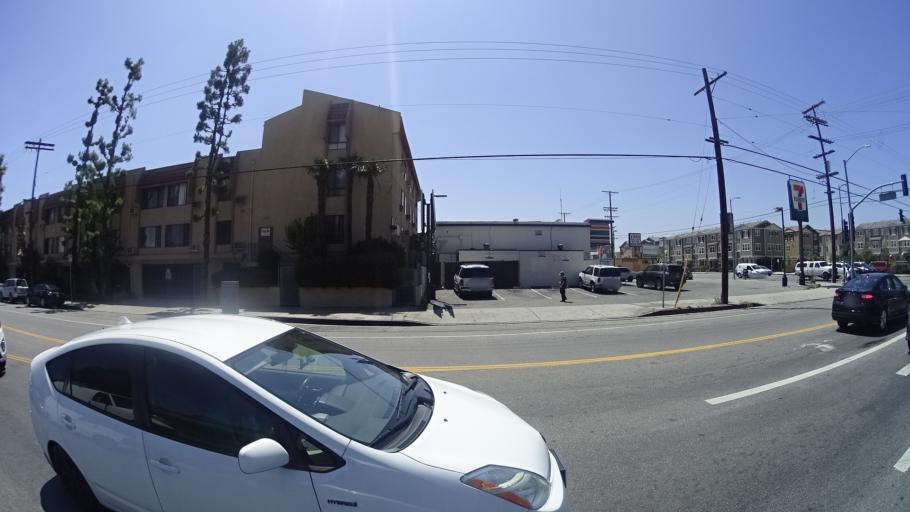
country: US
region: California
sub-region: Los Angeles County
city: Van Nuys
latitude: 34.2008
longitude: -118.4400
